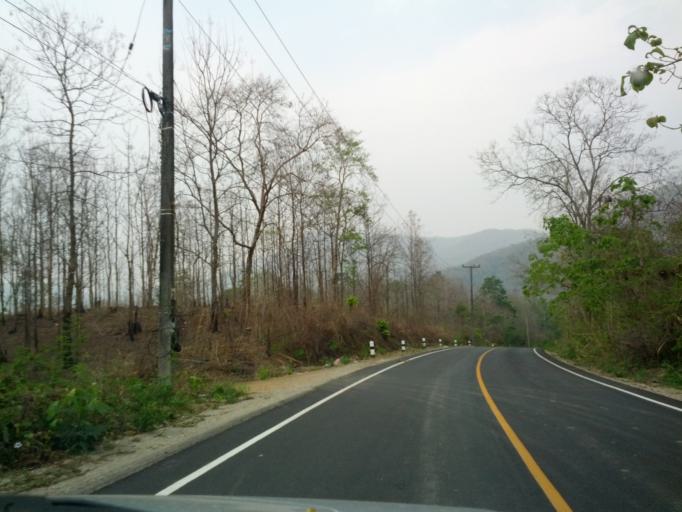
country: TH
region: Chiang Mai
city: Mae Taeng
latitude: 19.1024
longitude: 99.0777
